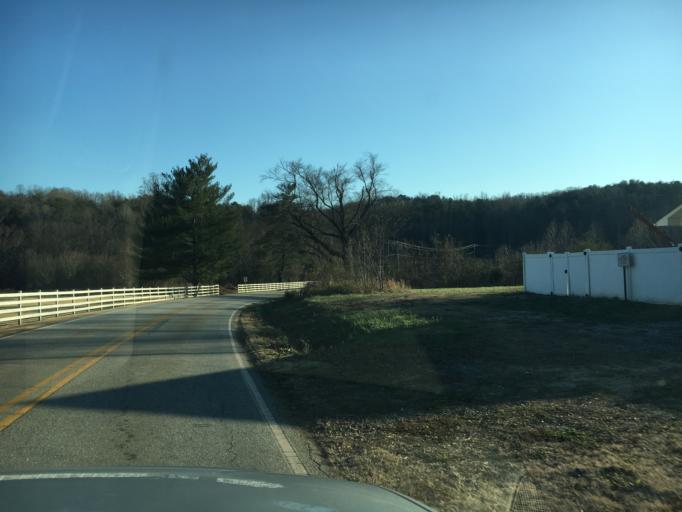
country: US
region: North Carolina
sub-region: Rutherford County
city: Rutherfordton
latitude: 35.2966
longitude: -81.9847
